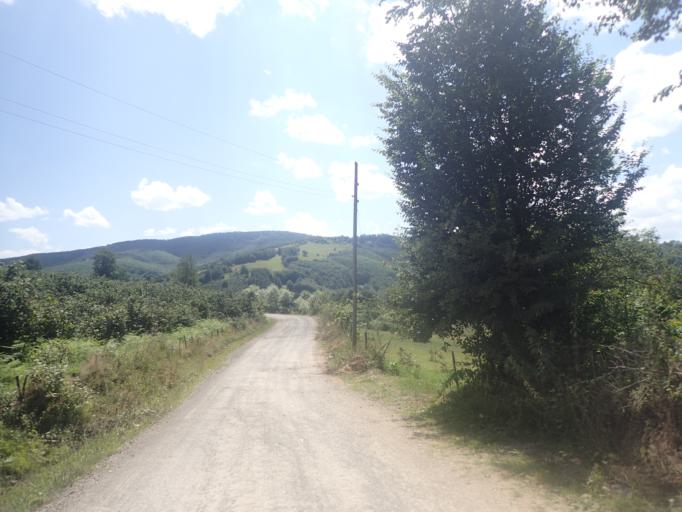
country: TR
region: Ordu
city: Aybasti
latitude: 40.6847
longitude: 37.3203
